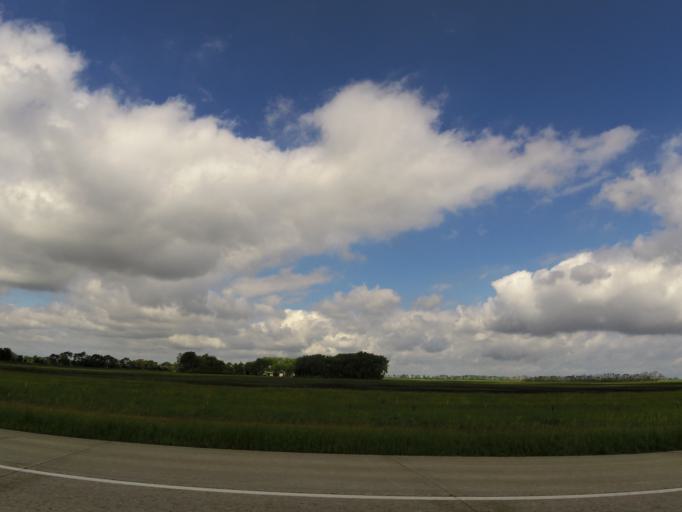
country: US
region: North Dakota
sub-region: Grand Forks County
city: Grand Forks
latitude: 48.1490
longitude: -97.1908
